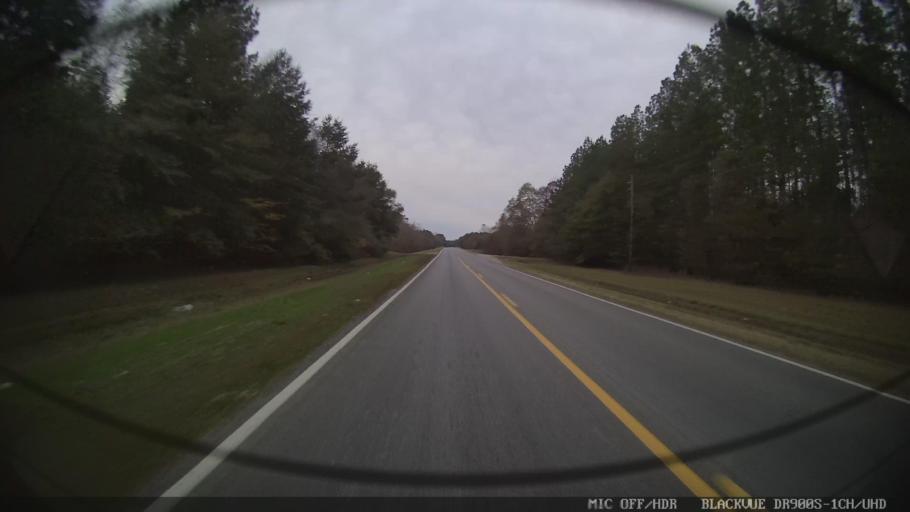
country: US
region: Mississippi
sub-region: Clarke County
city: Quitman
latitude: 32.0283
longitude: -88.8338
